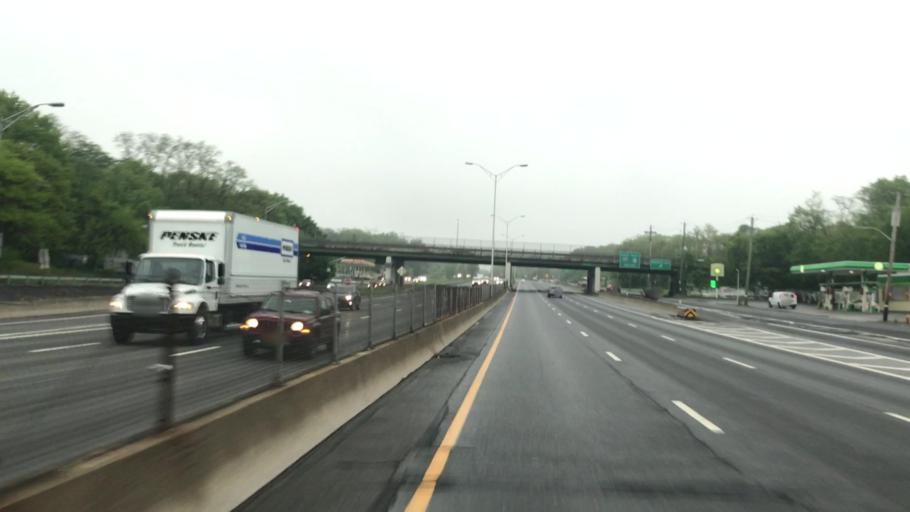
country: US
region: New York
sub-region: Westchester County
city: Bronxville
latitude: 40.9332
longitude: -73.8563
